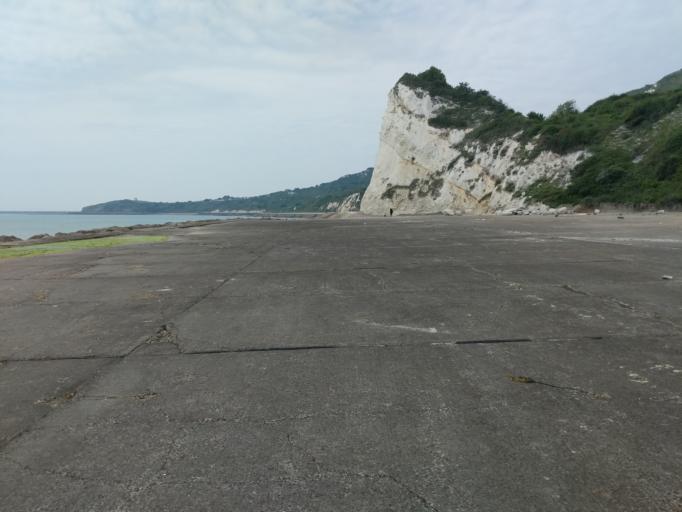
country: GB
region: England
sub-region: Kent
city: Folkestone
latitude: 51.0986
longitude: 1.2230
